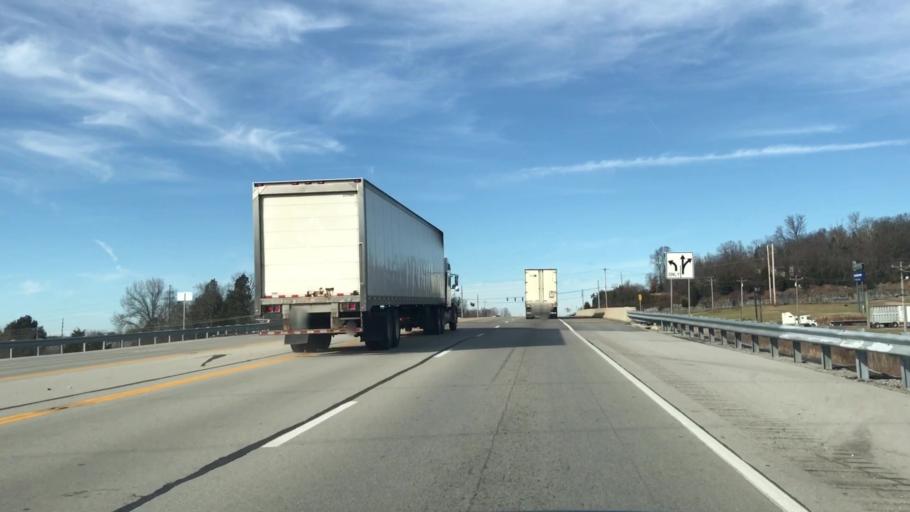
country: US
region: Kentucky
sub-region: Pulaski County
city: Somerset
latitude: 37.0484
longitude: -84.5859
